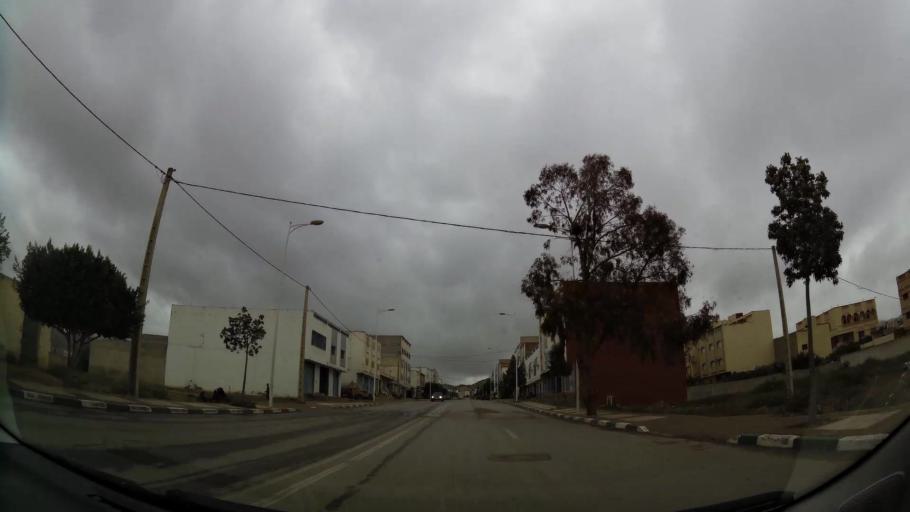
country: MA
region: Oriental
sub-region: Nador
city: Midar
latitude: 35.0504
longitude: -3.4602
